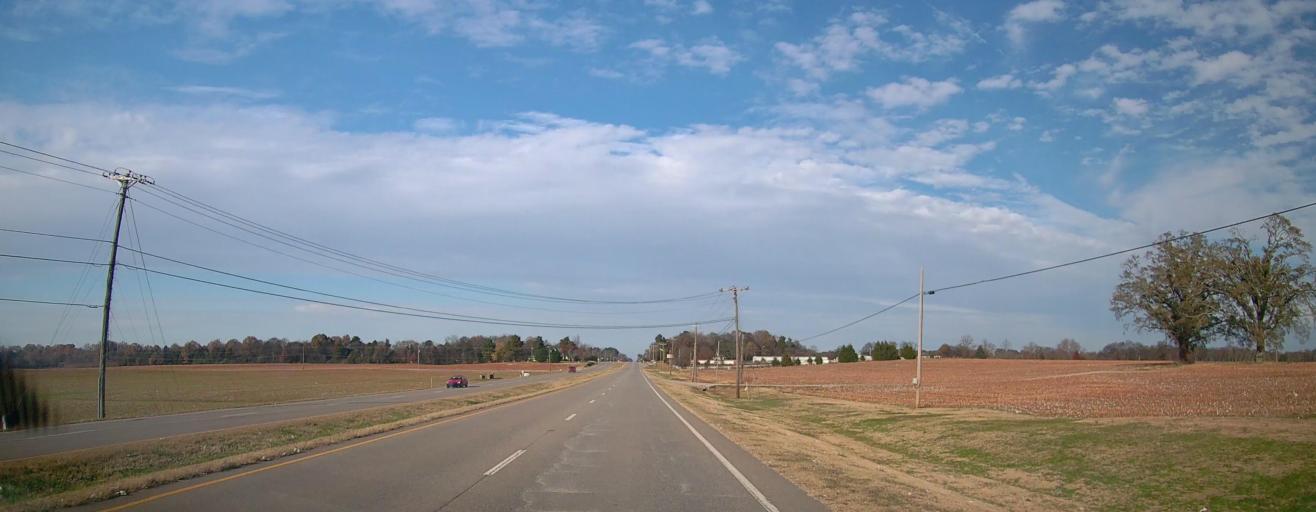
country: US
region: Alabama
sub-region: Limestone County
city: Athens
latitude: 34.7429
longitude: -86.9570
